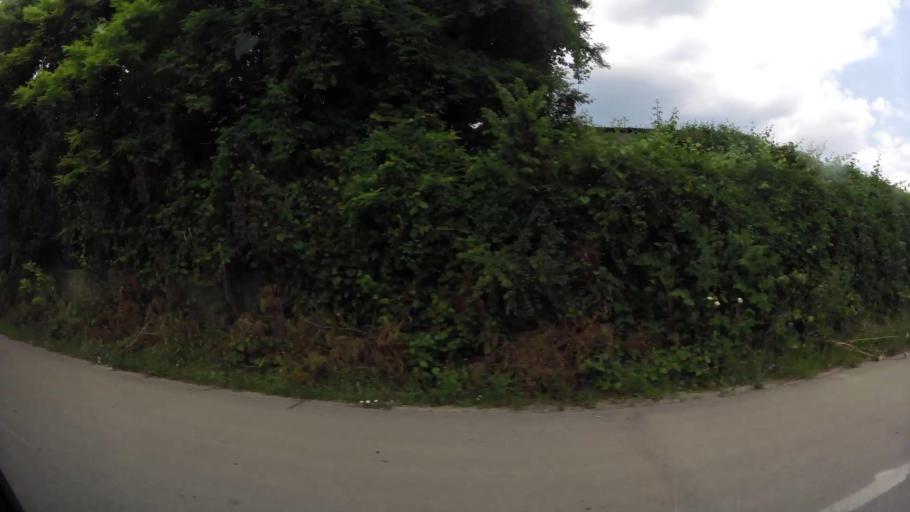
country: GR
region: West Macedonia
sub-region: Nomos Kozanis
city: Koila
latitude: 40.3389
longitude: 21.8248
